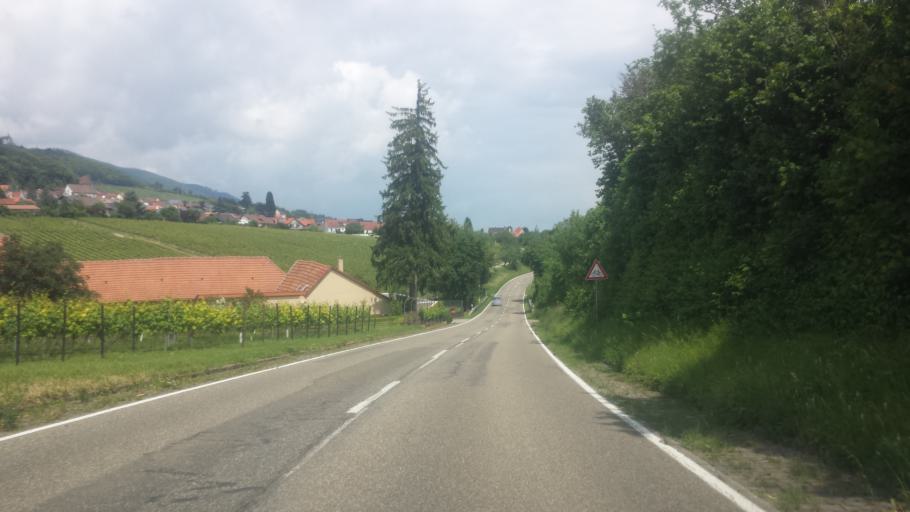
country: DE
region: Rheinland-Pfalz
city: Frankweiler
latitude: 49.2344
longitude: 8.0640
